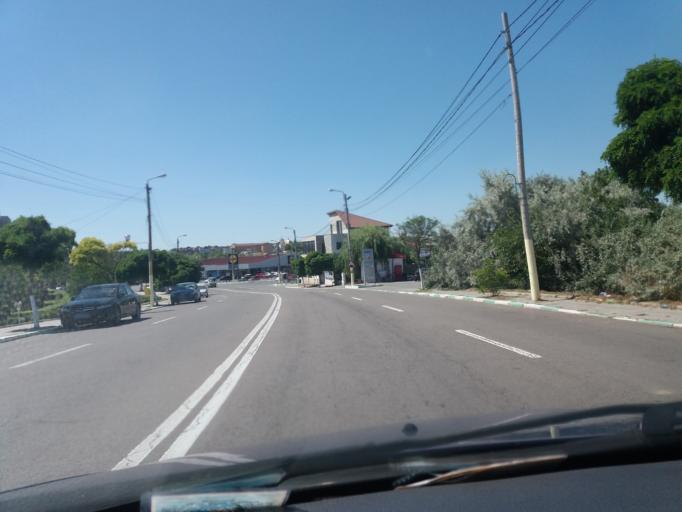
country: RO
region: Constanta
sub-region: Comuna Navodari
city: Navodari
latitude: 44.3240
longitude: 28.6170
